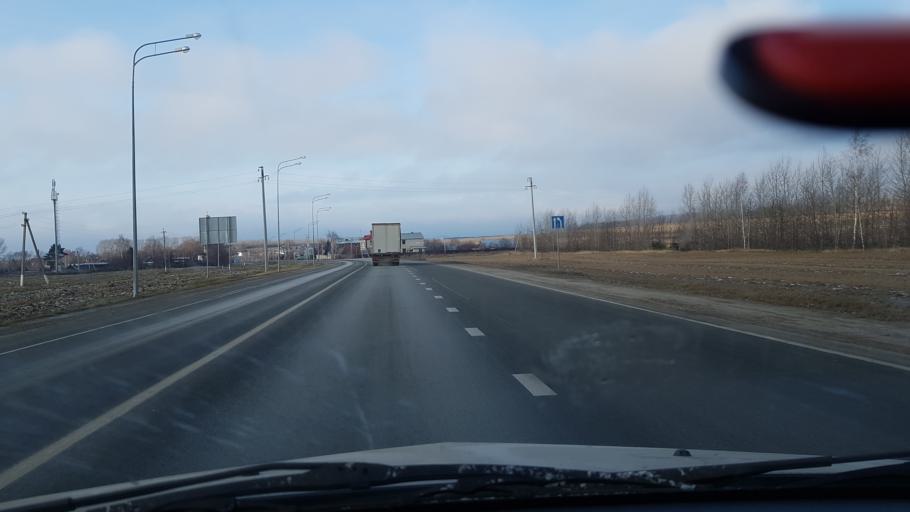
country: RU
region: Tatarstan
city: Laishevo
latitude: 55.3914
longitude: 49.8078
